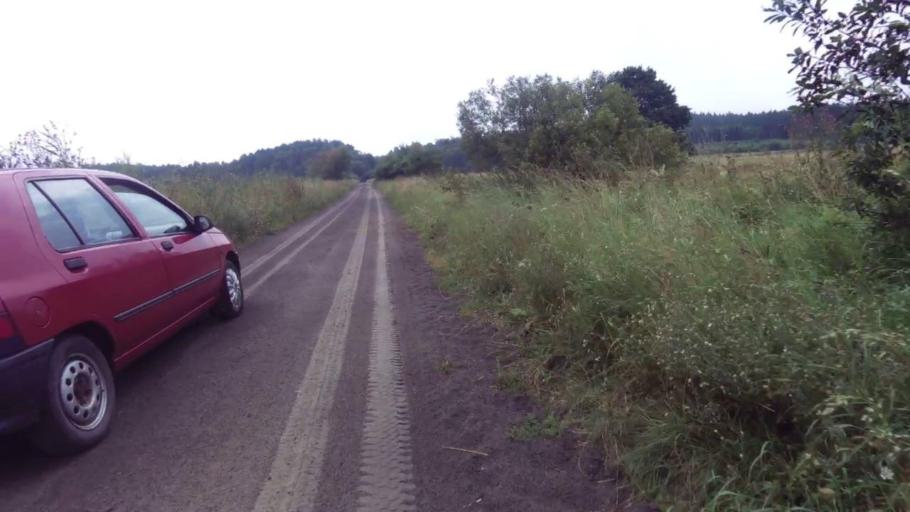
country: PL
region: West Pomeranian Voivodeship
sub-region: Powiat stargardzki
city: Suchan
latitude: 53.2473
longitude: 15.3843
